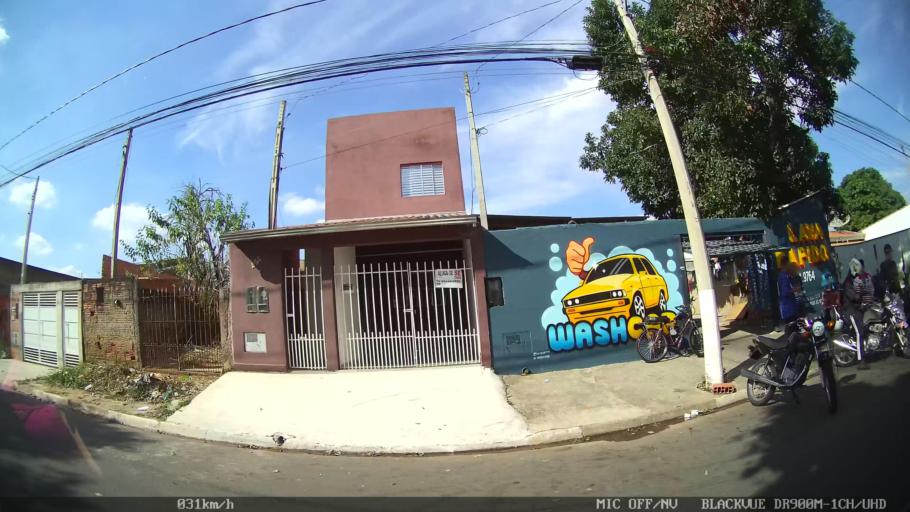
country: BR
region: Sao Paulo
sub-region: Hortolandia
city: Hortolandia
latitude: -22.9013
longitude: -47.2341
